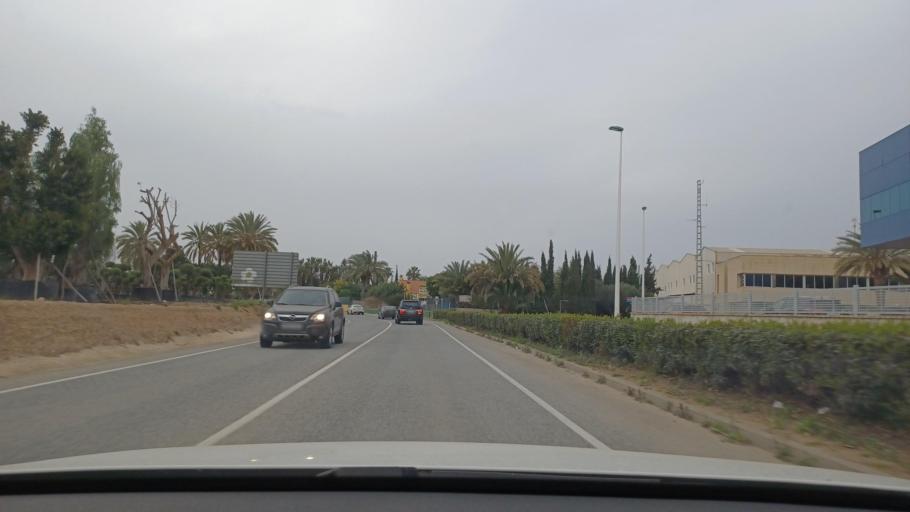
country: ES
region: Valencia
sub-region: Provincia de Alicante
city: Elche
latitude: 38.2426
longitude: -0.6861
